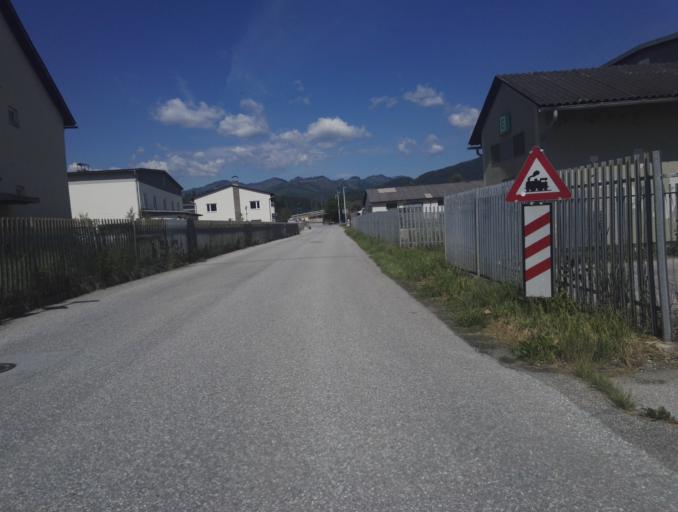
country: AT
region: Styria
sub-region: Politischer Bezirk Graz-Umgebung
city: Gratkorn
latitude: 47.1250
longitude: 15.3356
